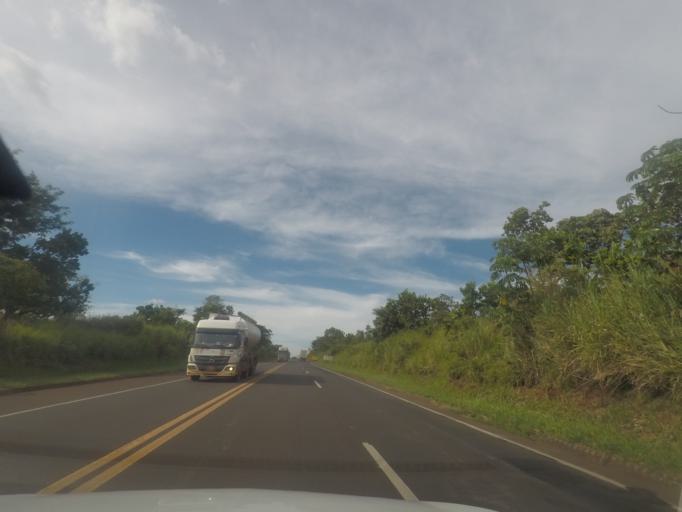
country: BR
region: Minas Gerais
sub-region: Monte Alegre De Minas
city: Monte Alegre de Minas
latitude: -19.0325
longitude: -49.0114
